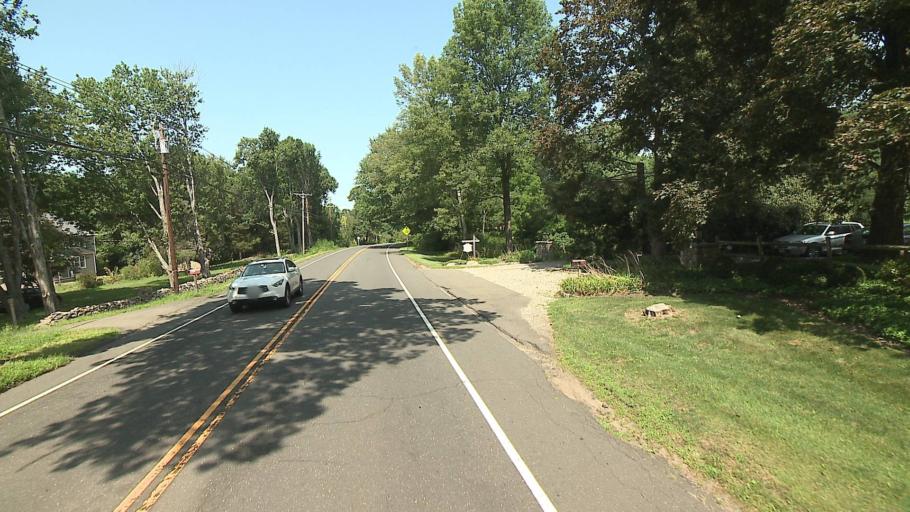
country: US
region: Connecticut
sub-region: Fairfield County
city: Trumbull
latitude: 41.2686
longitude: -73.2950
